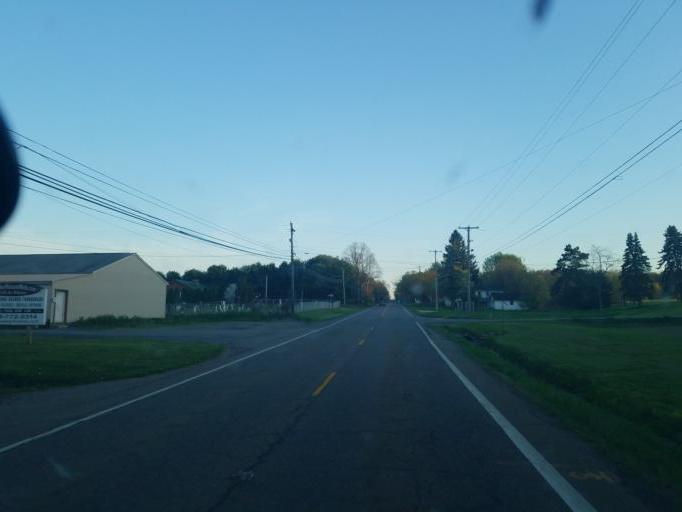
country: US
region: Ohio
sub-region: Trumbull County
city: Brookfield Center
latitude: 41.3511
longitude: -80.5694
